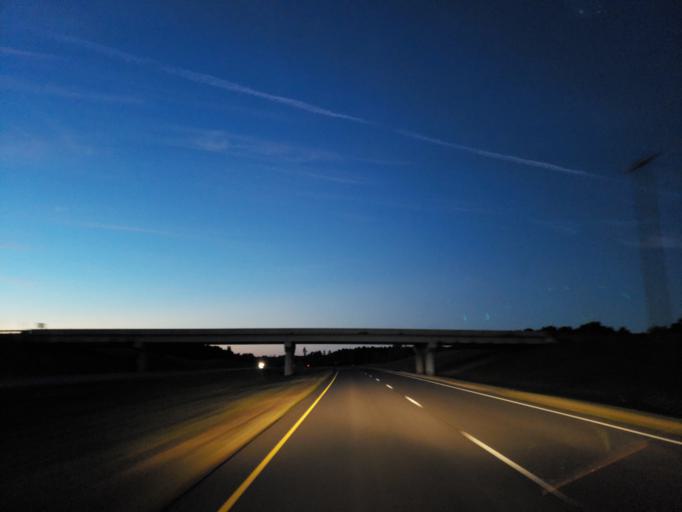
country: US
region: Mississippi
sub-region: Clarke County
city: Quitman
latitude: 32.0583
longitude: -88.6778
